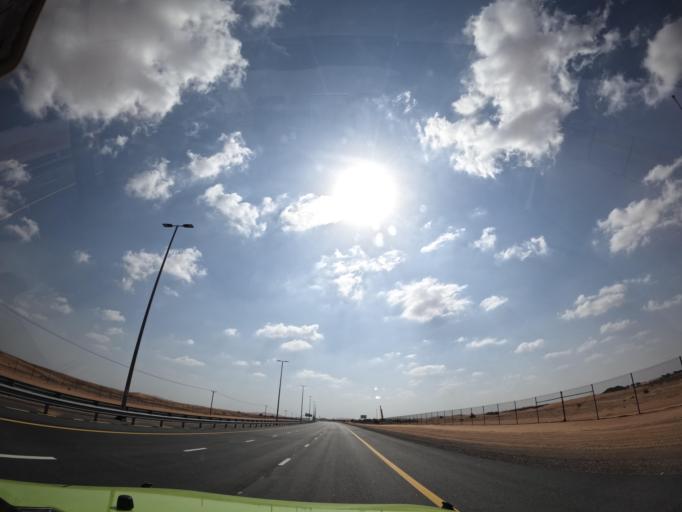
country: AE
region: Ash Shariqah
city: Adh Dhayd
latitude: 24.9794
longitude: 55.6793
